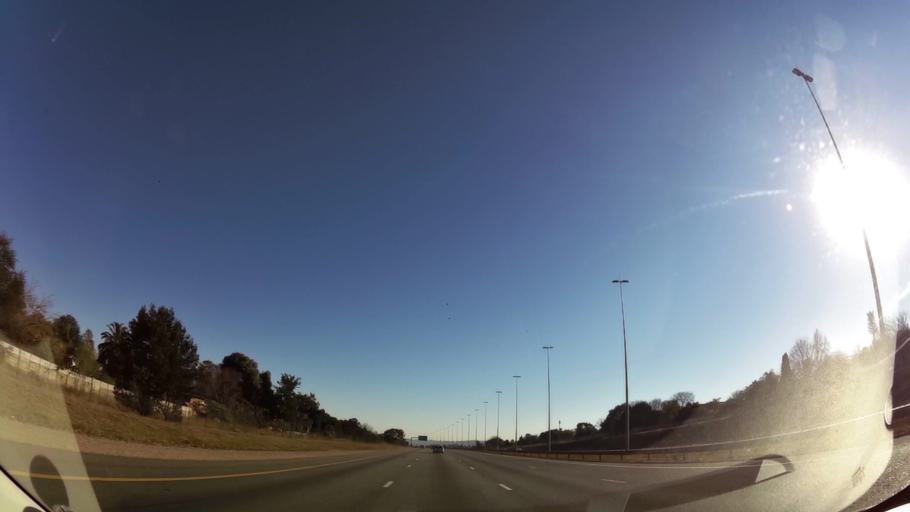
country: ZA
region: Gauteng
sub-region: City of Tshwane Metropolitan Municipality
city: Centurion
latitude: -25.8425
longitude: 28.2493
